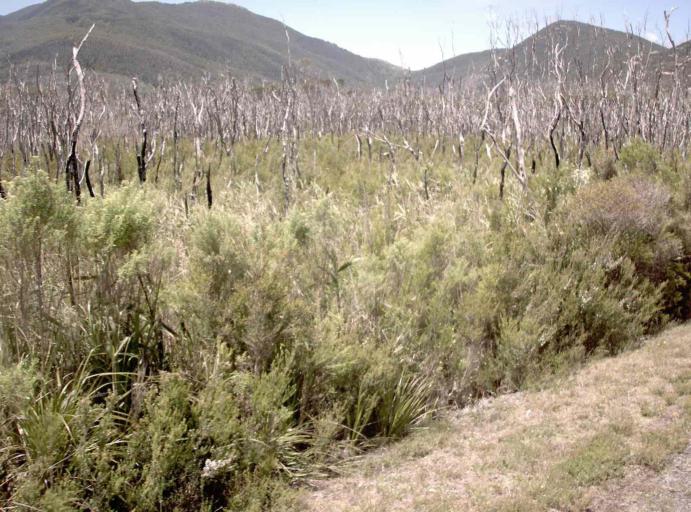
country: AU
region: Victoria
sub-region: Latrobe
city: Morwell
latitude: -39.0249
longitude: 146.3310
